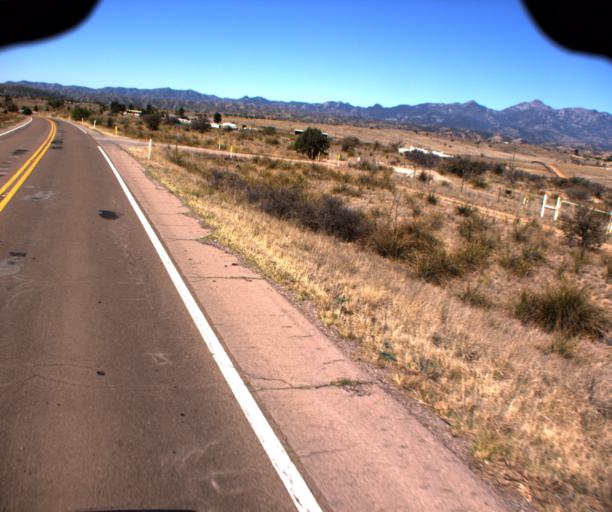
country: US
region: Arizona
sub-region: Pima County
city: Corona de Tucson
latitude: 31.6767
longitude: -110.6657
